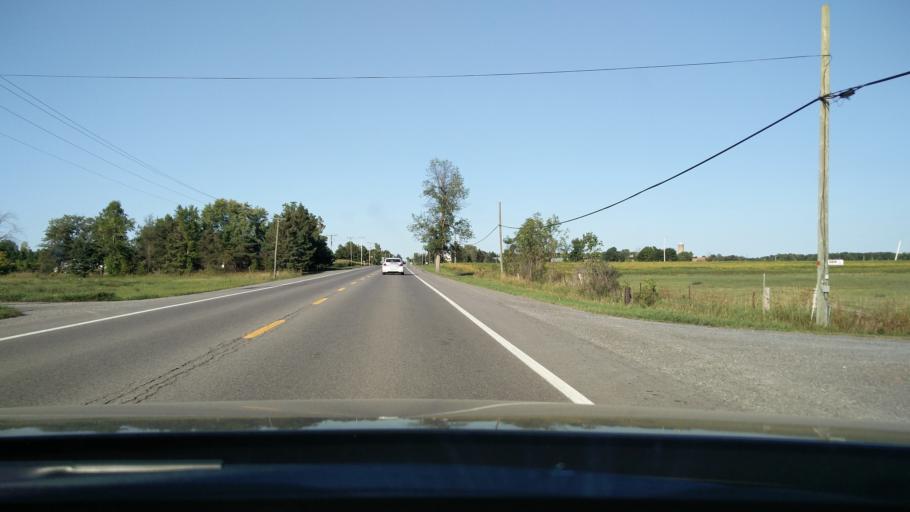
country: CA
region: Ontario
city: Bells Corners
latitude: 45.1410
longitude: -75.9231
